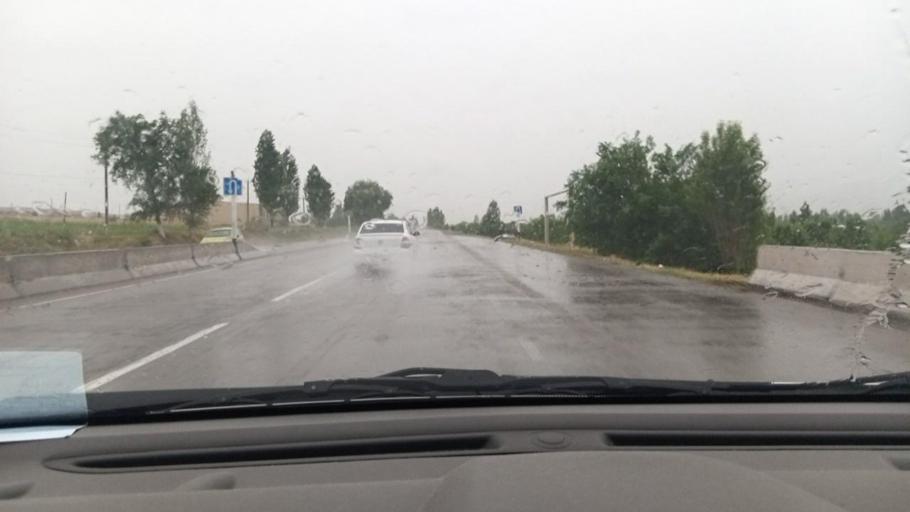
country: UZ
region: Toshkent
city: Angren
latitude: 40.9705
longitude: 69.9867
